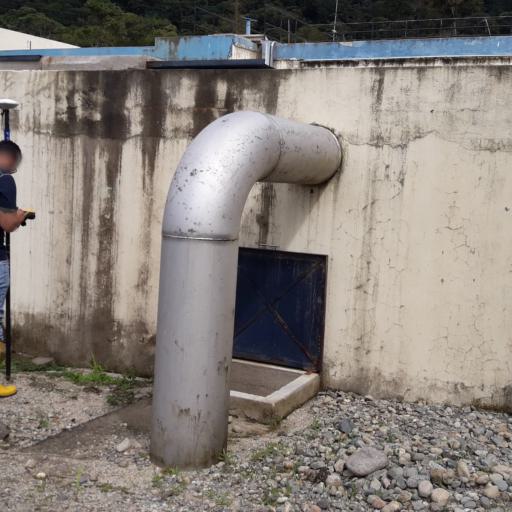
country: EC
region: Napo
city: Archidona
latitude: -0.9459
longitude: -77.8908
